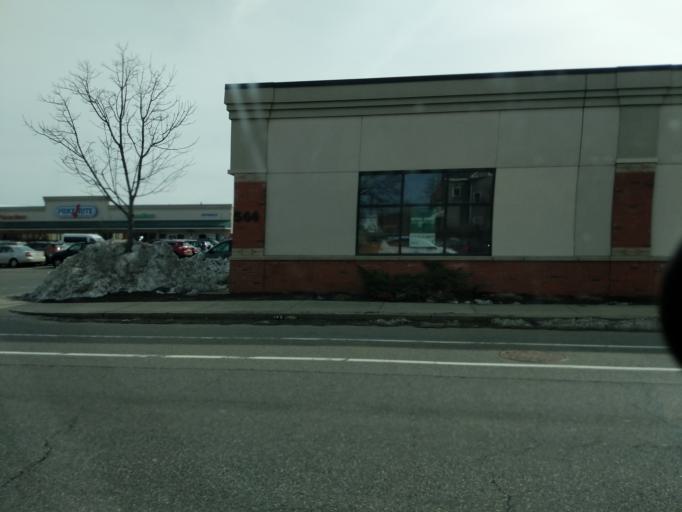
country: US
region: Massachusetts
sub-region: Worcester County
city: Worcester
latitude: 42.2469
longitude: -71.8103
